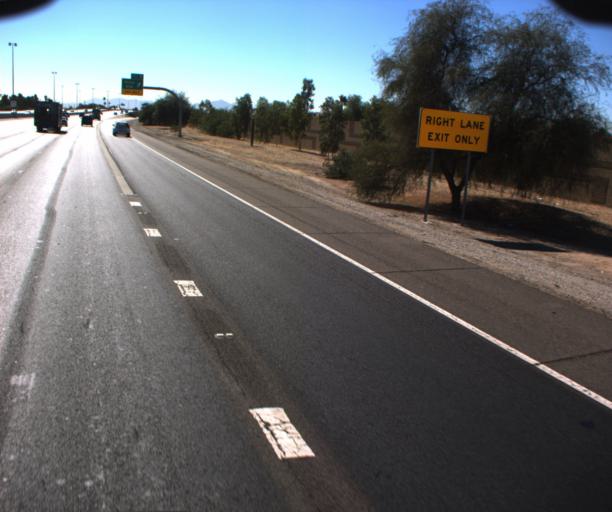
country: US
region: Arizona
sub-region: Maricopa County
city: Peoria
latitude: 33.5732
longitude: -112.2578
